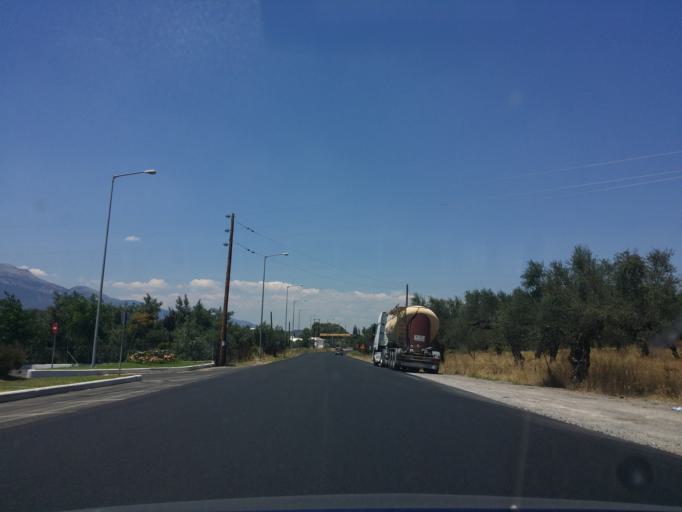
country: GR
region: Peloponnese
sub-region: Nomos Lakonias
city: Sparti
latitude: 37.0765
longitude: 22.4491
